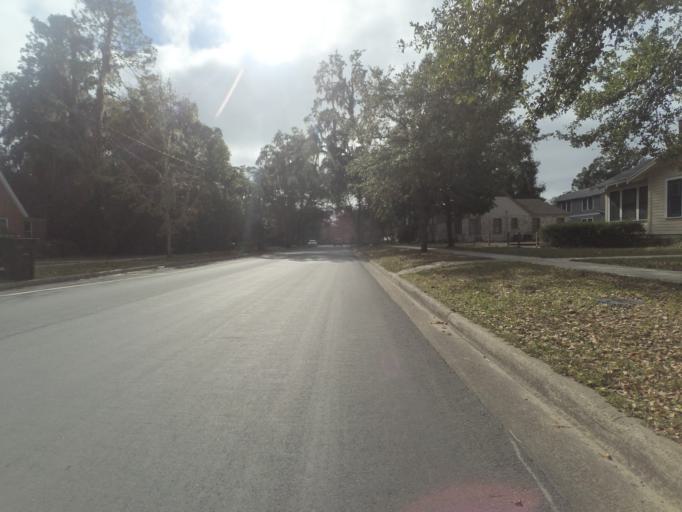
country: US
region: Florida
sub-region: Alachua County
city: Gainesville
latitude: 29.6476
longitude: -82.3351
